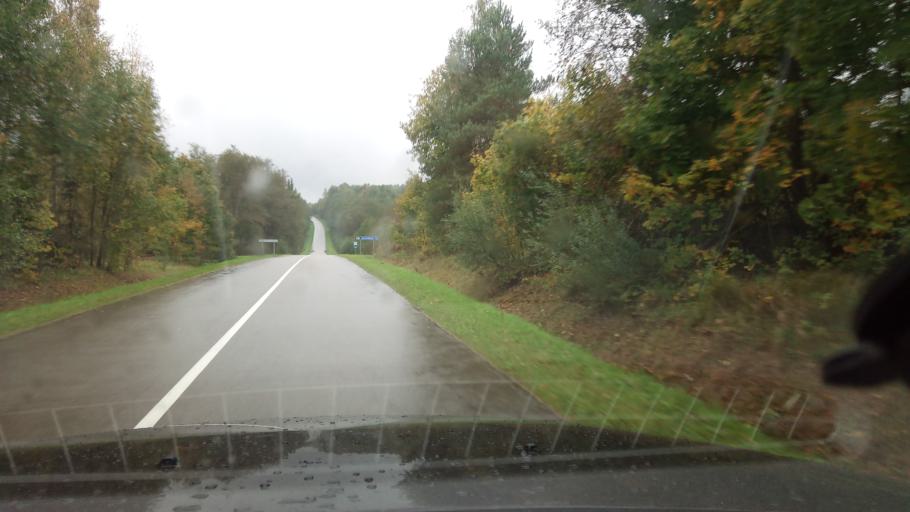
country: LT
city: Skaidiskes
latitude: 54.5615
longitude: 25.5018
